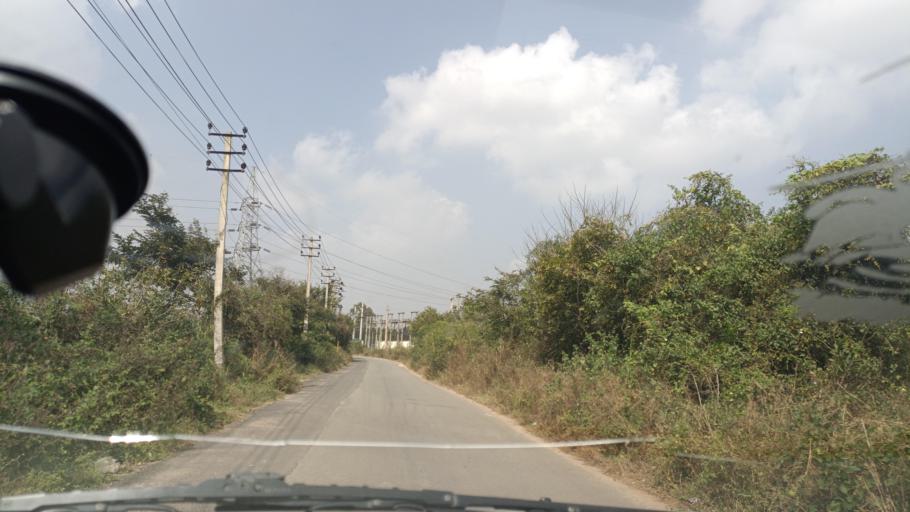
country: IN
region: Karnataka
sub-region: Bangalore Urban
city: Yelahanka
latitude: 13.1519
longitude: 77.6319
